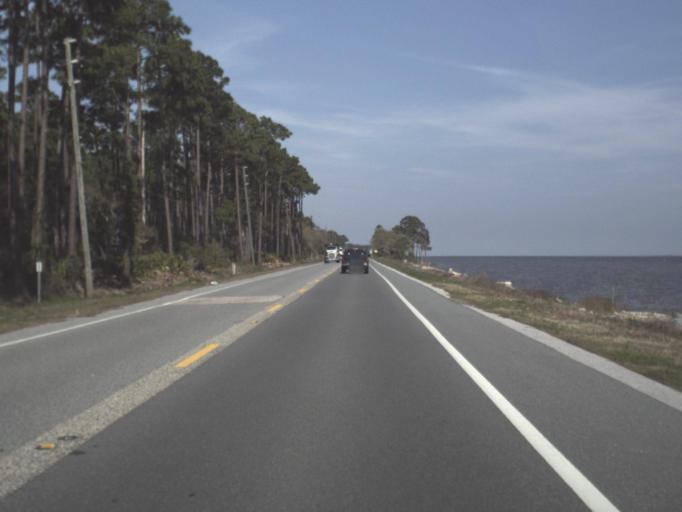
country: US
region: Florida
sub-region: Franklin County
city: Eastpoint
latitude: 29.7595
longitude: -84.8222
